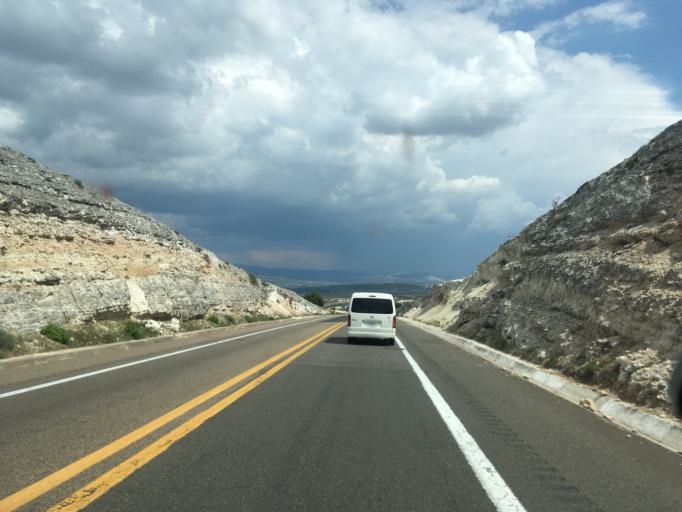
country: MX
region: Oaxaca
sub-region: Villa Tejupam de la Union
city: Villa Tejupam de la Union
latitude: 17.8241
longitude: -97.3702
